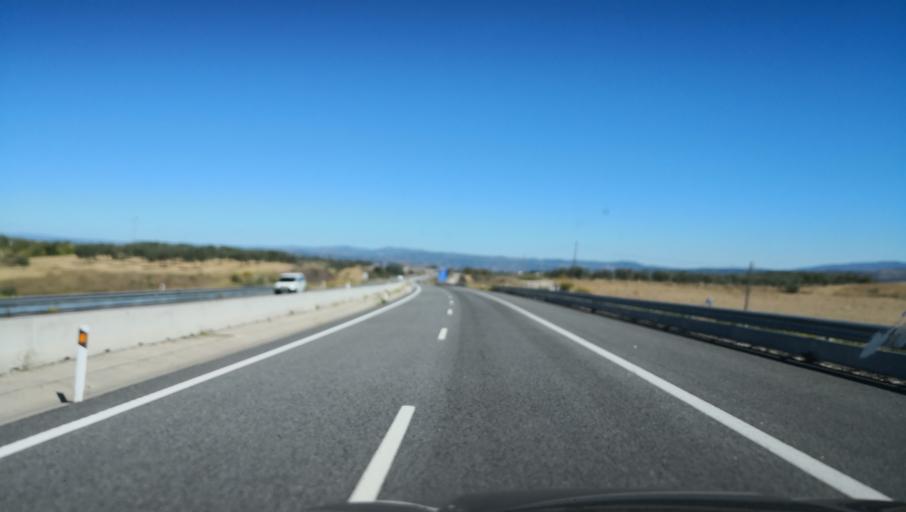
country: PT
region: Braganca
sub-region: Mirandela
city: Mirandela
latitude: 41.4642
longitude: -7.2471
